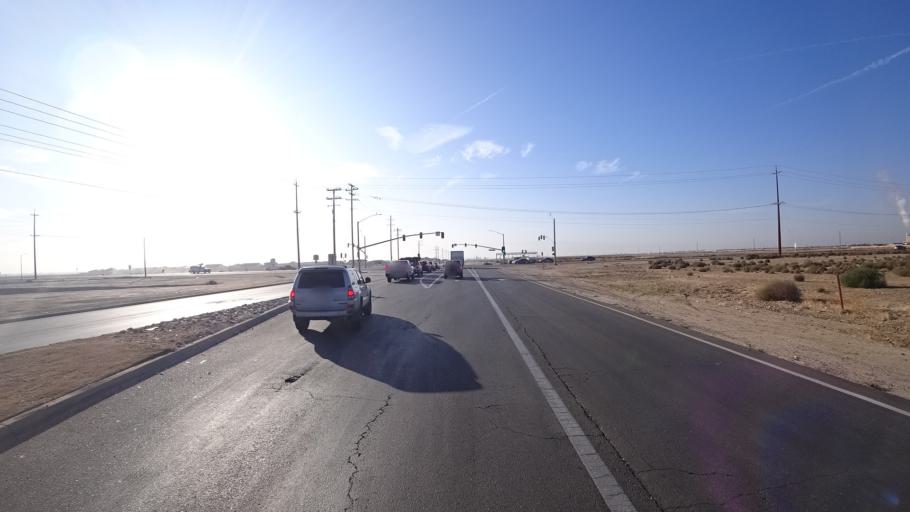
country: US
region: California
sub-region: Kern County
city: Greenacres
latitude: 35.2970
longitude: -119.0922
